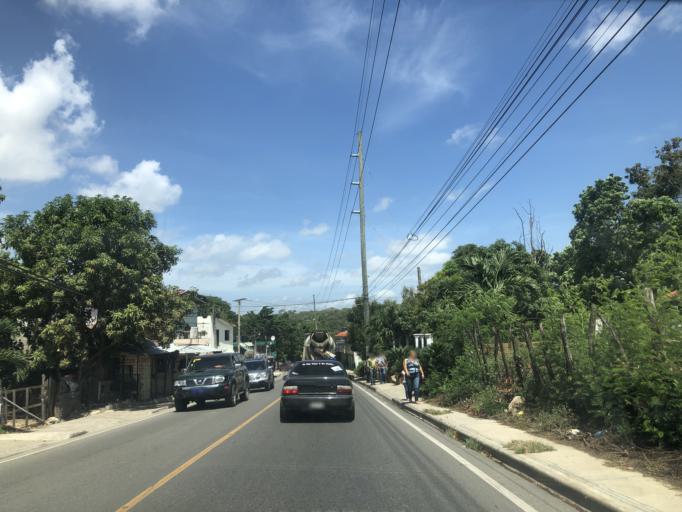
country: DO
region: Santiago
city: La Canela
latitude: 19.4525
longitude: -70.7617
